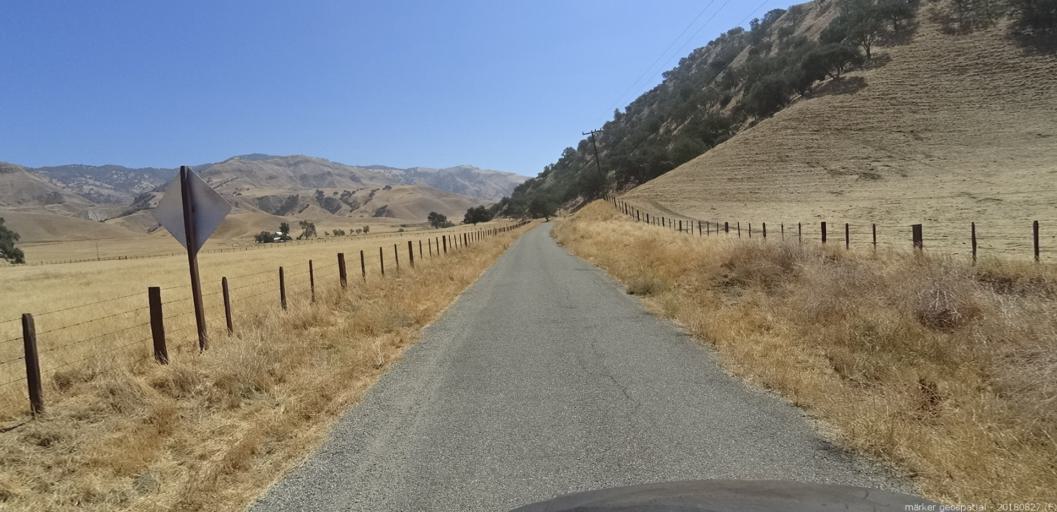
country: US
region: California
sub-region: Monterey County
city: King City
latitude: 36.3089
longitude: -120.9232
